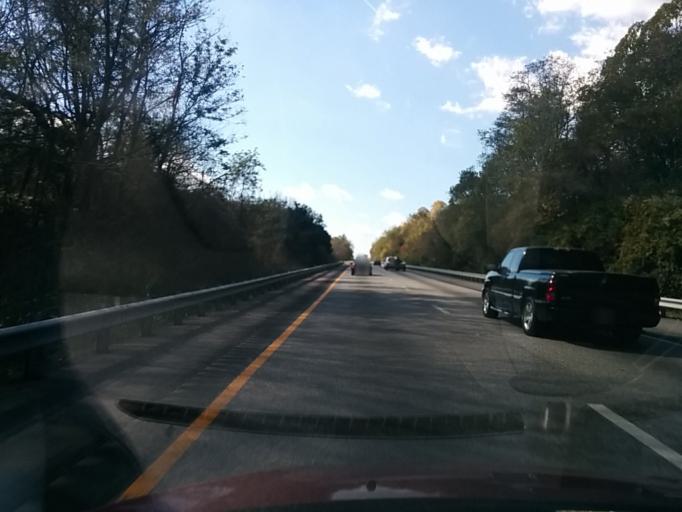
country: US
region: Virginia
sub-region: Botetourt County
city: Daleville
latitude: 37.4267
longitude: -79.8778
